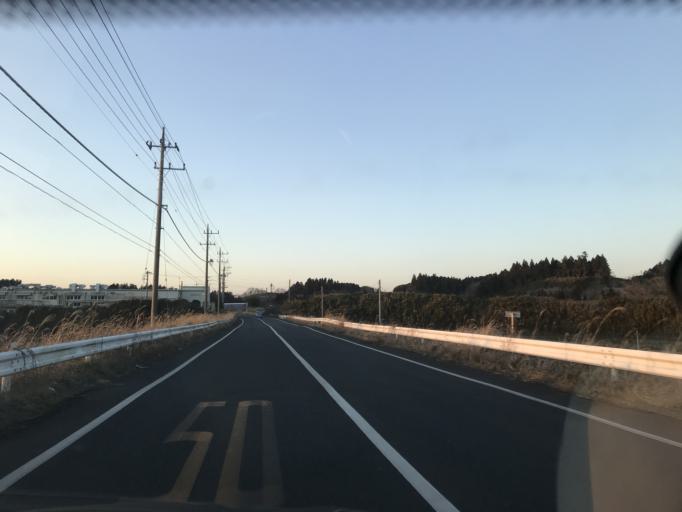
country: JP
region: Chiba
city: Sawara
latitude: 35.8182
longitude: 140.5194
